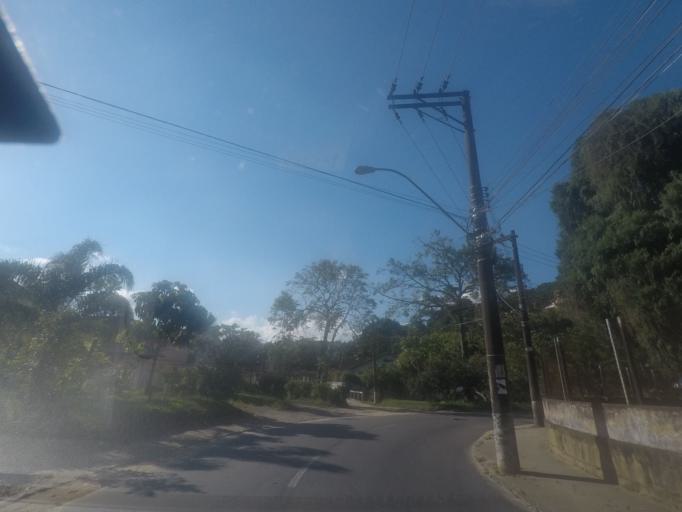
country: BR
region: Rio de Janeiro
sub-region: Petropolis
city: Petropolis
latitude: -22.5160
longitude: -43.1692
